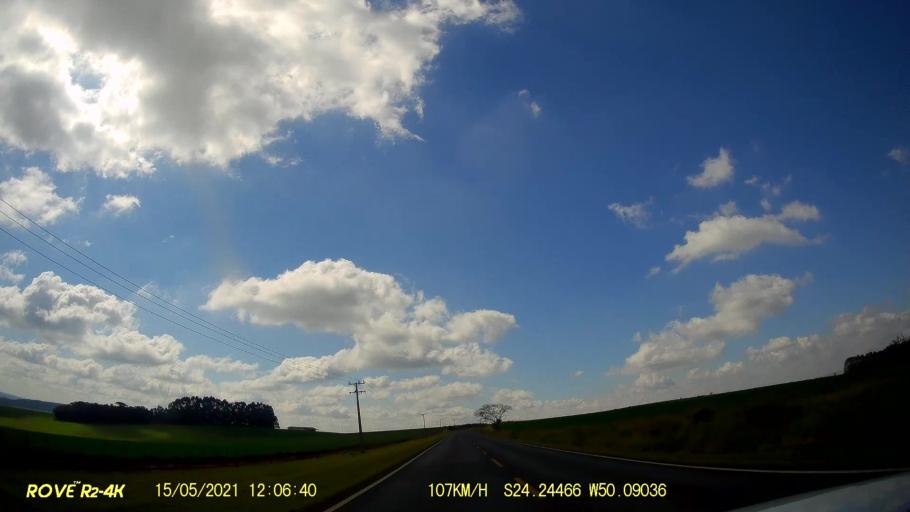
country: BR
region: Parana
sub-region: Pirai Do Sul
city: Pirai do Sul
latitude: -24.2446
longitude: -50.0903
